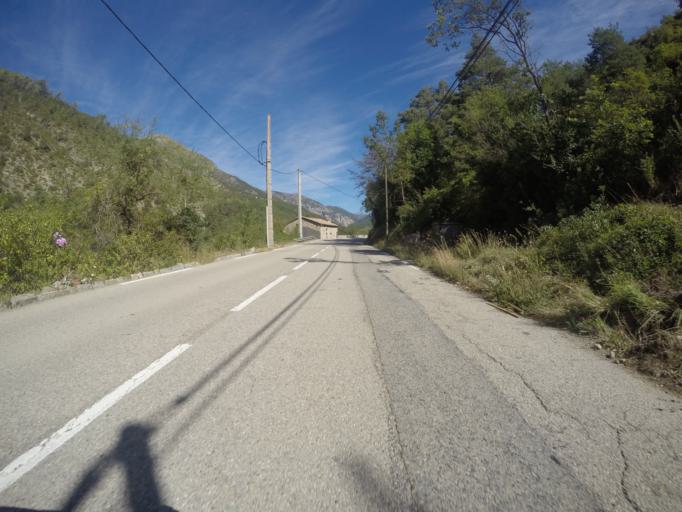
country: FR
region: Provence-Alpes-Cote d'Azur
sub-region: Departement des Alpes-Maritimes
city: Gilette
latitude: 43.9473
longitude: 7.1603
